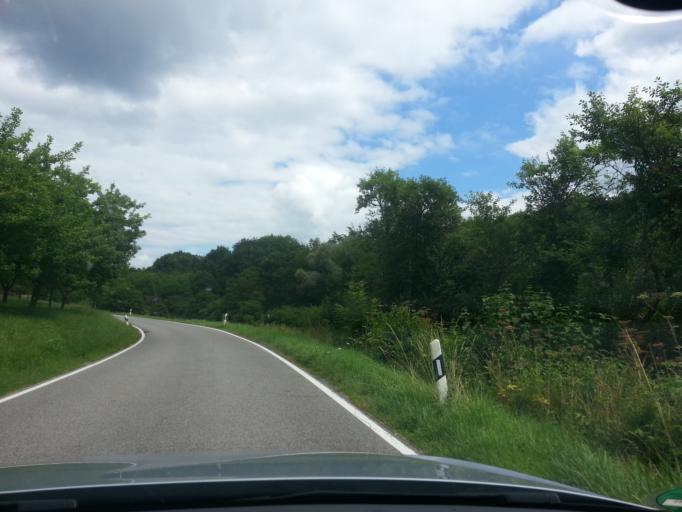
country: DE
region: Saarland
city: Beckingen
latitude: 49.4374
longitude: 6.6905
